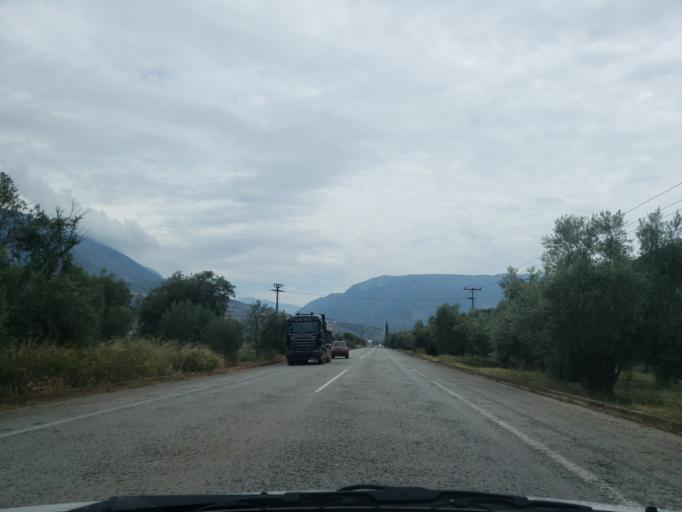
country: GR
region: Central Greece
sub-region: Nomos Fokidos
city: Itea
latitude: 38.4825
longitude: 22.4284
